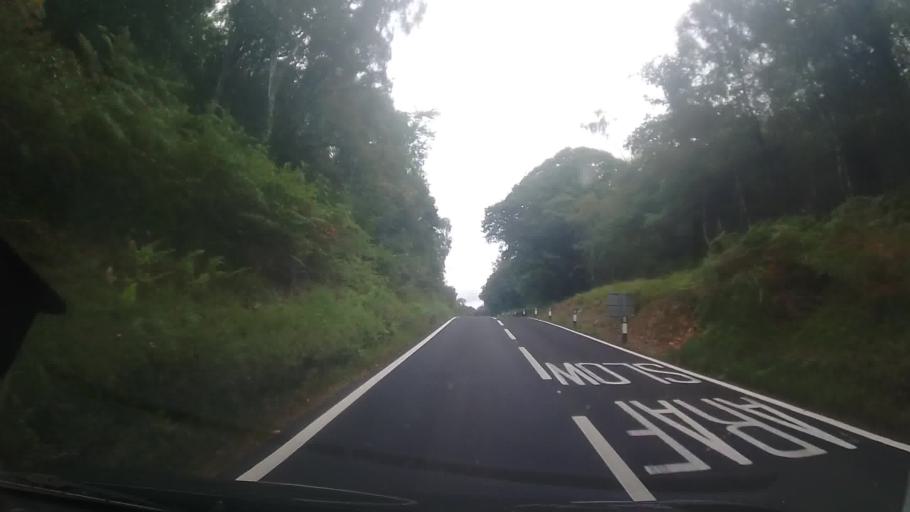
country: GB
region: Wales
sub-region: County of Ceredigion
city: Bow Street
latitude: 52.5200
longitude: -3.9699
